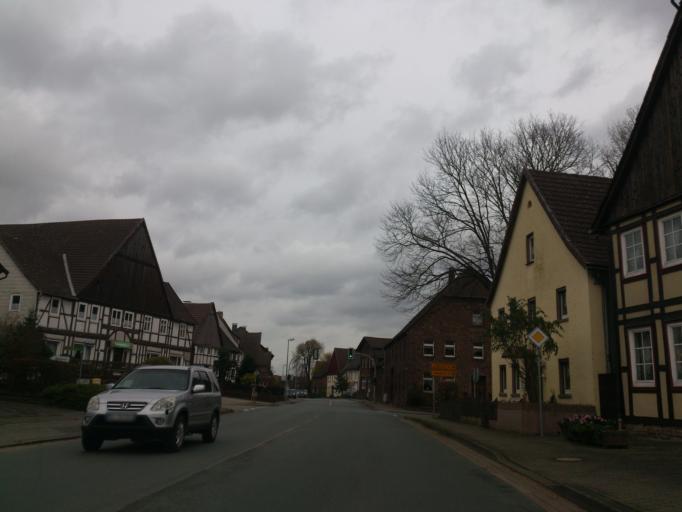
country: DE
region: Lower Saxony
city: Boffzen
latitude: 51.7333
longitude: 9.3615
